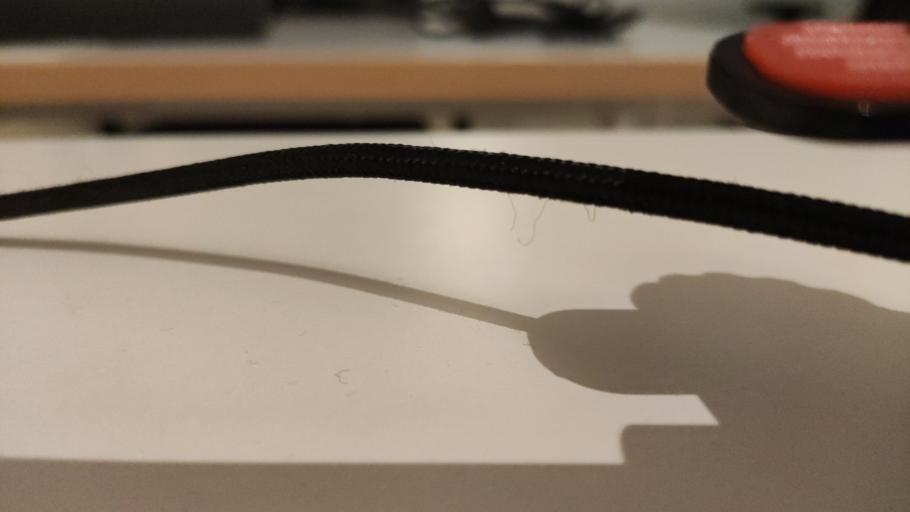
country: RU
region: Moskovskaya
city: Orekhovo-Zuyevo
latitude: 55.8034
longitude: 38.9732
